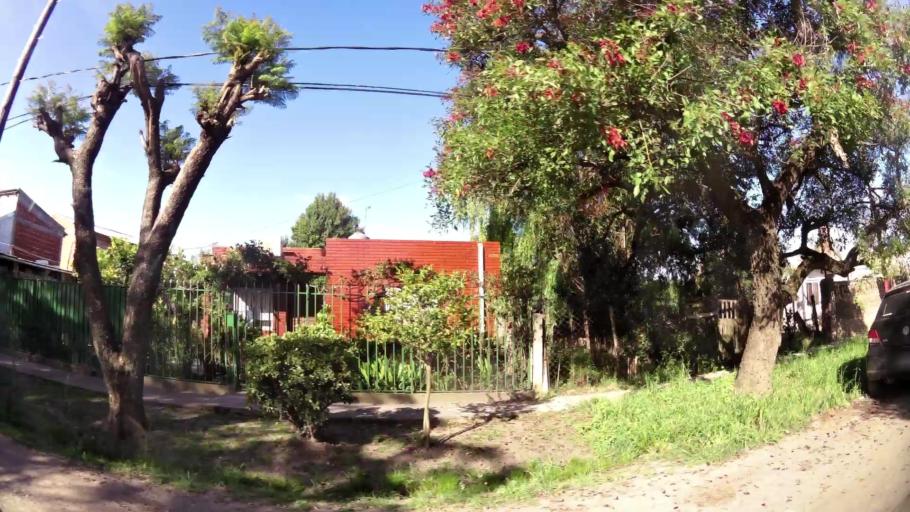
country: AR
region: Buenos Aires
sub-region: Partido de Almirante Brown
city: Adrogue
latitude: -34.8231
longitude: -58.3593
